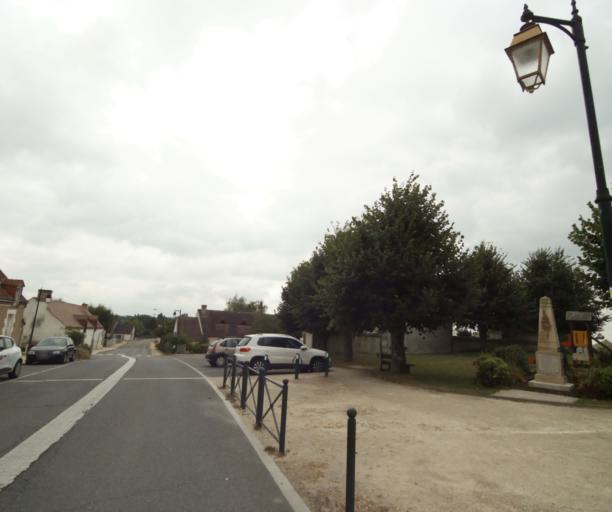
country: FR
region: Centre
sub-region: Departement du Loiret
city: Marigny-les-Usages
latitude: 47.9572
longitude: 2.0149
